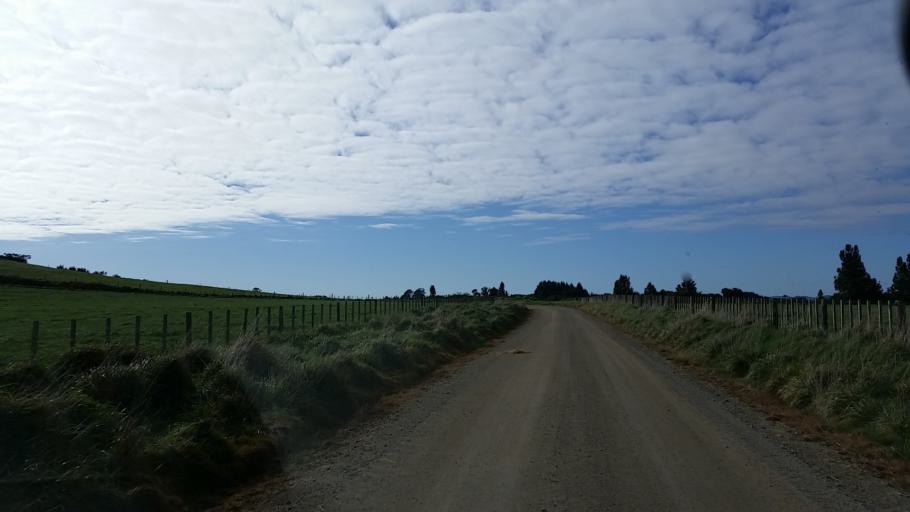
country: NZ
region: Taranaki
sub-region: South Taranaki District
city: Patea
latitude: -39.6925
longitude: 174.6582
